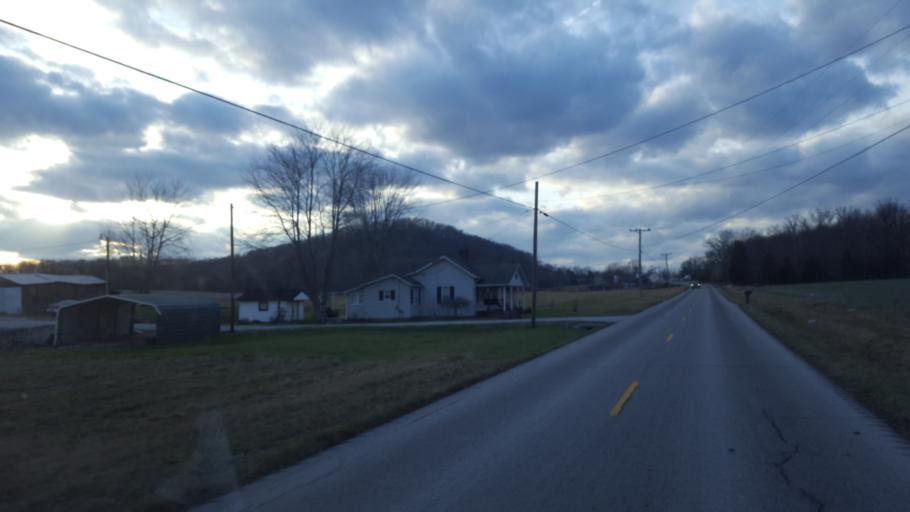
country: US
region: Kentucky
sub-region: Fleming County
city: Flemingsburg
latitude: 38.4761
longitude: -83.5971
